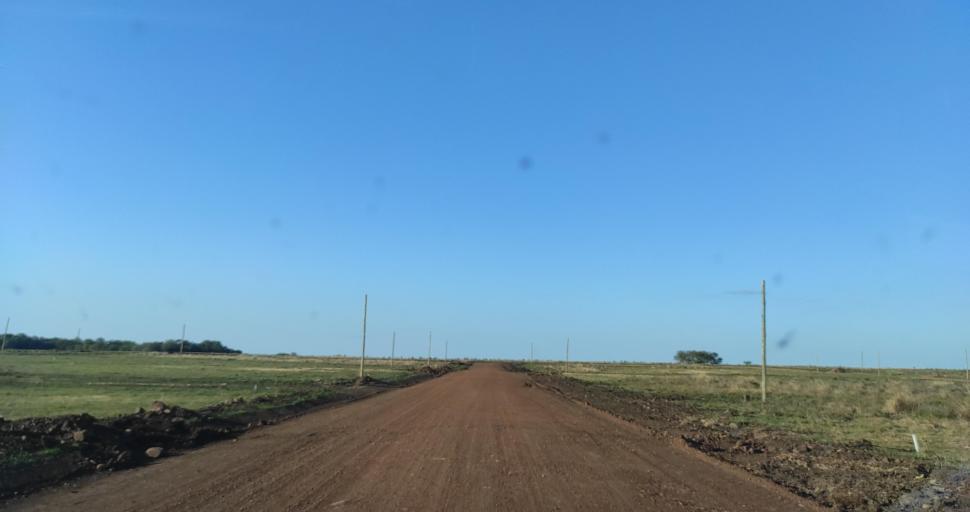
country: PY
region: Itapua
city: Carmen del Parana
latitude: -27.4104
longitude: -56.1817
